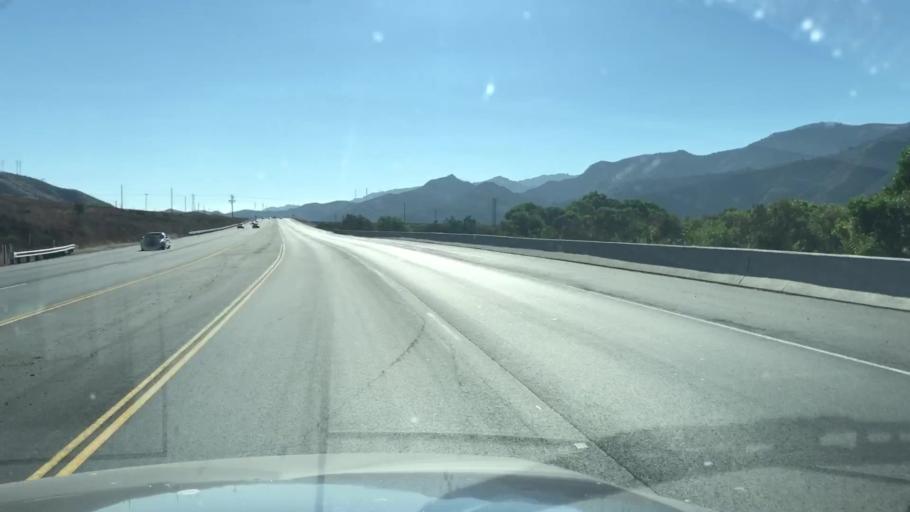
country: US
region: California
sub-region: Los Angeles County
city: Val Verde
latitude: 34.4044
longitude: -118.7166
